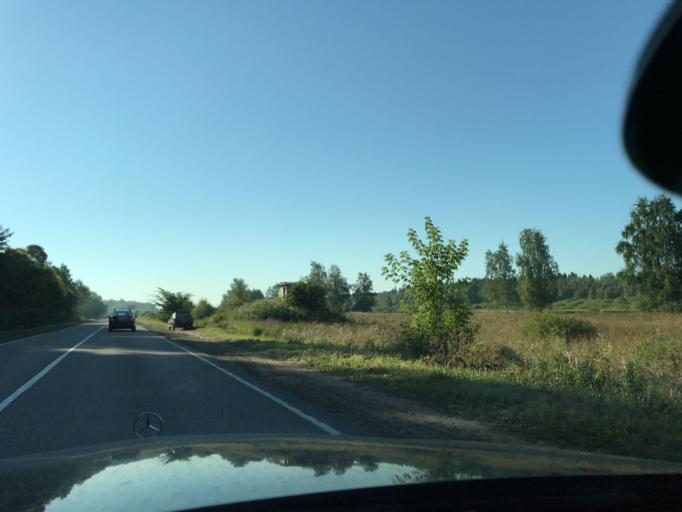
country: RU
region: Moskovskaya
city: Bakhchivandzhi
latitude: 55.8588
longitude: 38.0624
